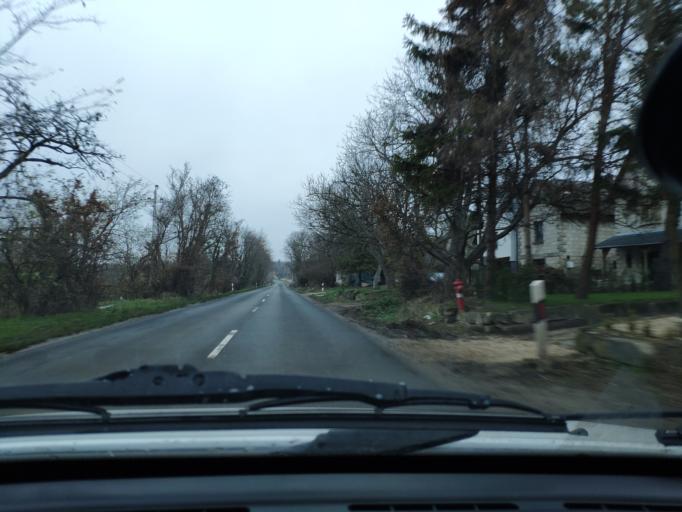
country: HU
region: Pest
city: Soskut
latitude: 47.4216
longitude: 18.8260
